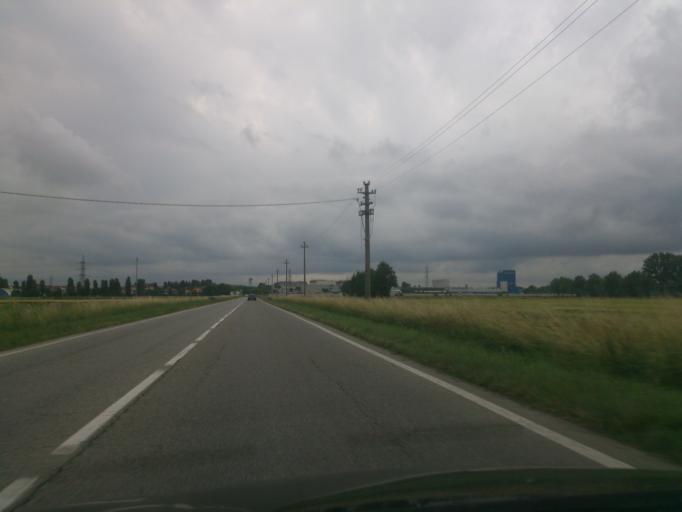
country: IT
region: Lombardy
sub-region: Citta metropolitana di Milano
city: Triginto
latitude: 45.4150
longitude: 9.3148
